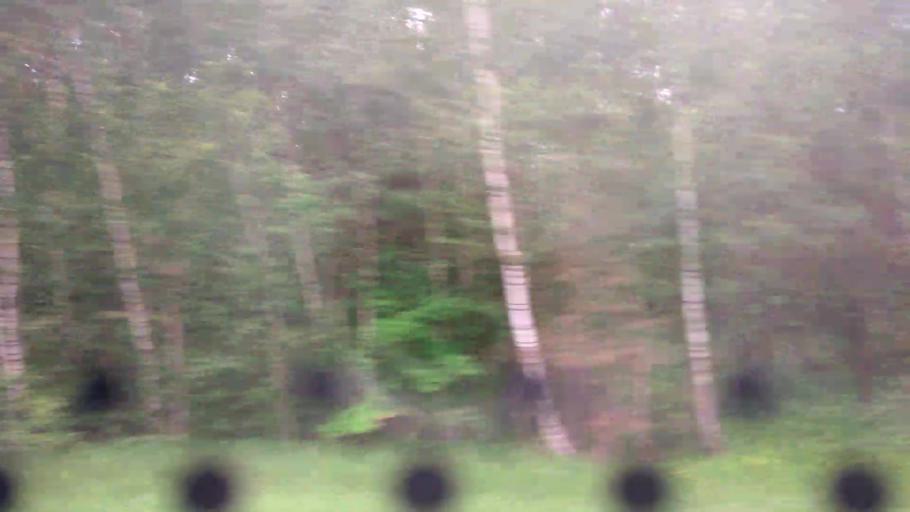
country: RU
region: Moskovskaya
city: Kolomna
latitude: 55.0523
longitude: 38.8707
